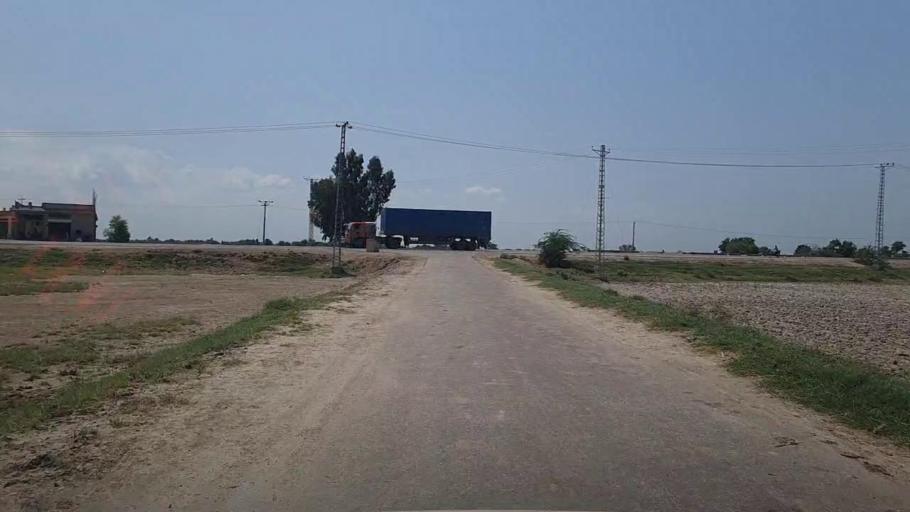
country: PK
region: Sindh
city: Ubauro
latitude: 28.1836
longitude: 69.8008
